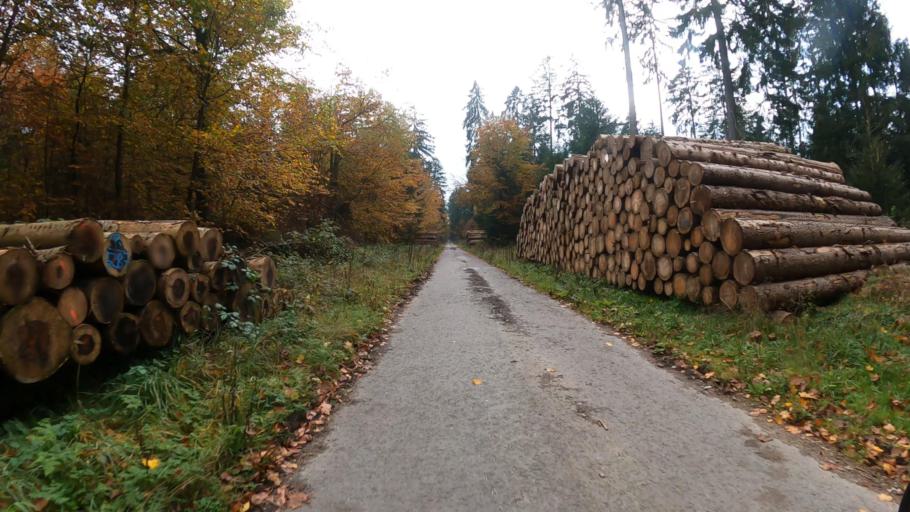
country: DE
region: Lower Saxony
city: Buchholz in der Nordheide
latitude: 53.3804
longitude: 9.8284
